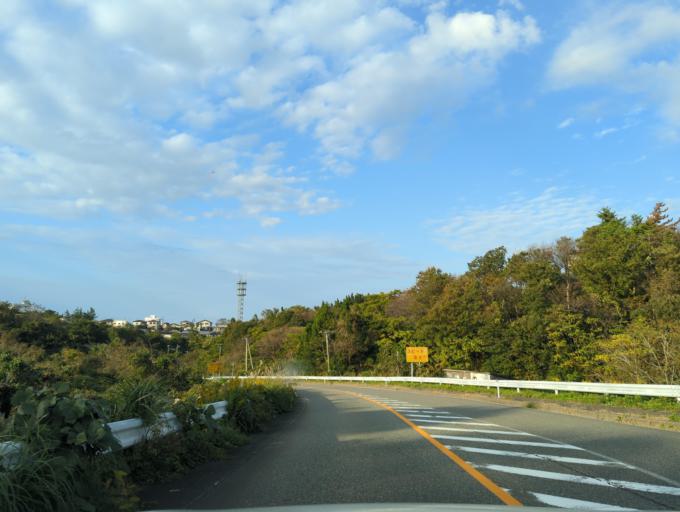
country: JP
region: Niigata
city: Kashiwazaki
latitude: 37.3587
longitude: 138.5325
